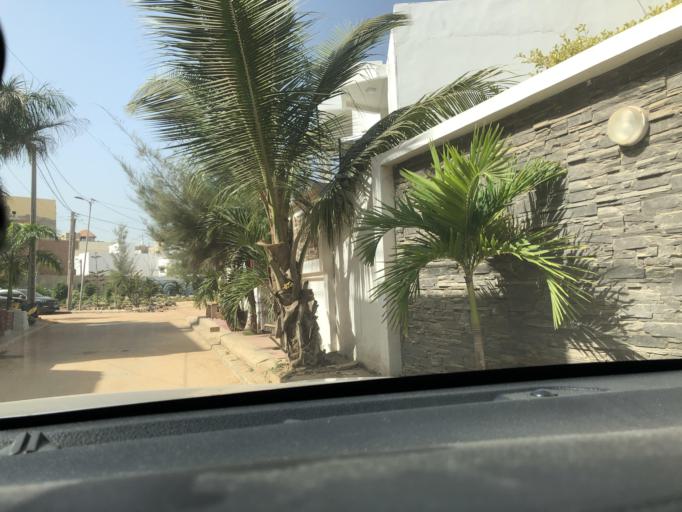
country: SN
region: Dakar
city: Mermoz Boabab
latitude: 14.7325
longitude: -17.4996
